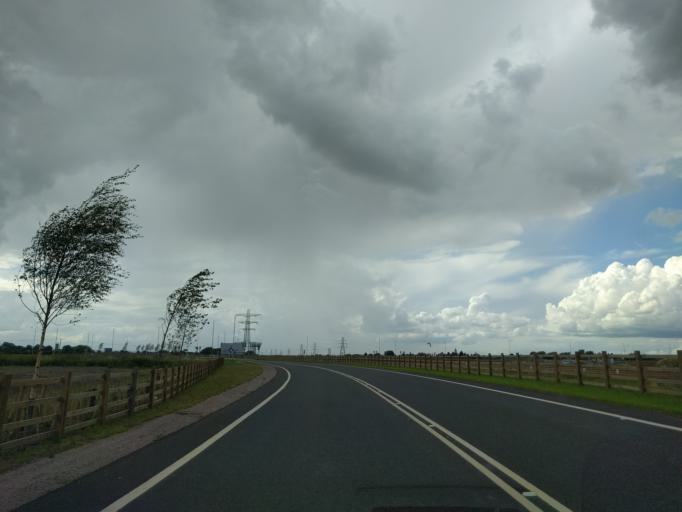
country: GB
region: England
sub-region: Nottinghamshire
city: Newark on Trent
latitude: 53.0524
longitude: -0.8029
